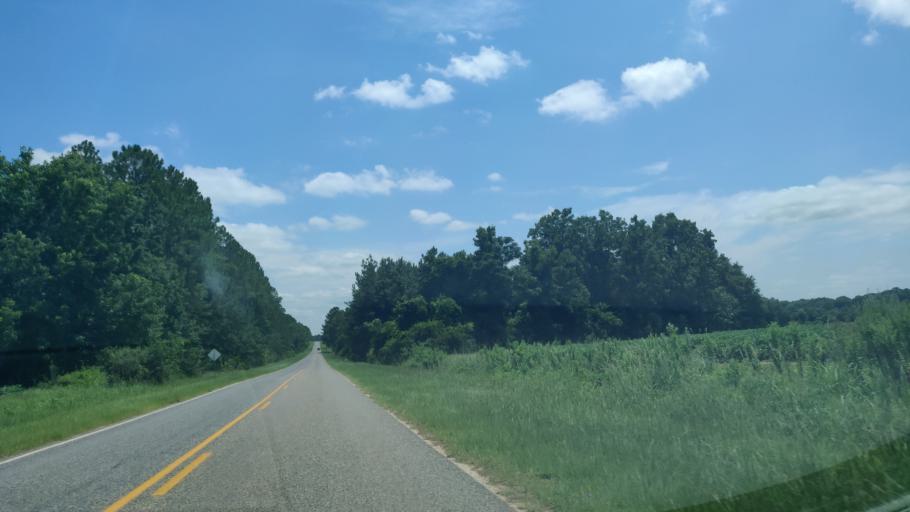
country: US
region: Georgia
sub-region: Tift County
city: Omega
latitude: 31.4591
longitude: -83.6375
